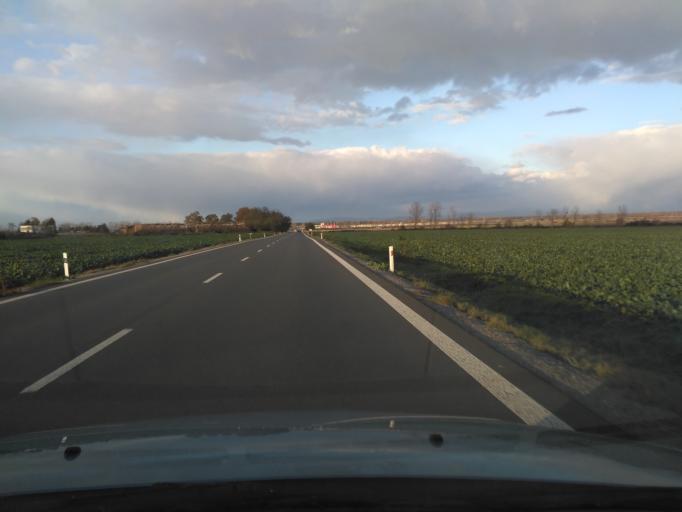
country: SK
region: Kosicky
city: Trebisov
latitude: 48.5876
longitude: 21.7095
